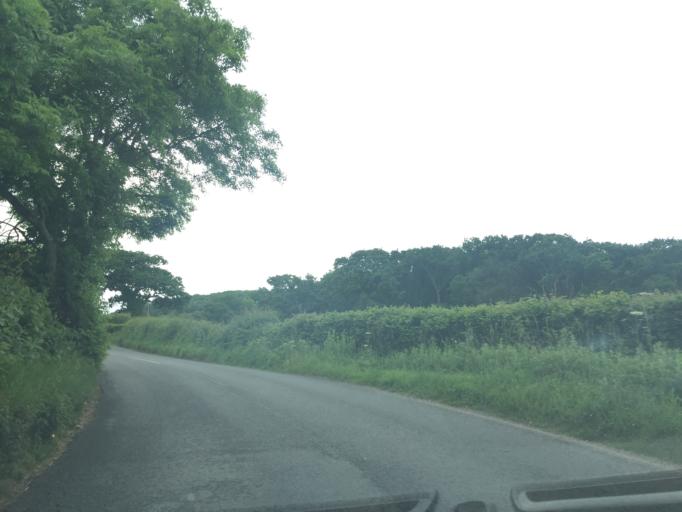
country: GB
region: England
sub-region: Dorset
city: Swanage
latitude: 50.6437
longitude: -2.0362
